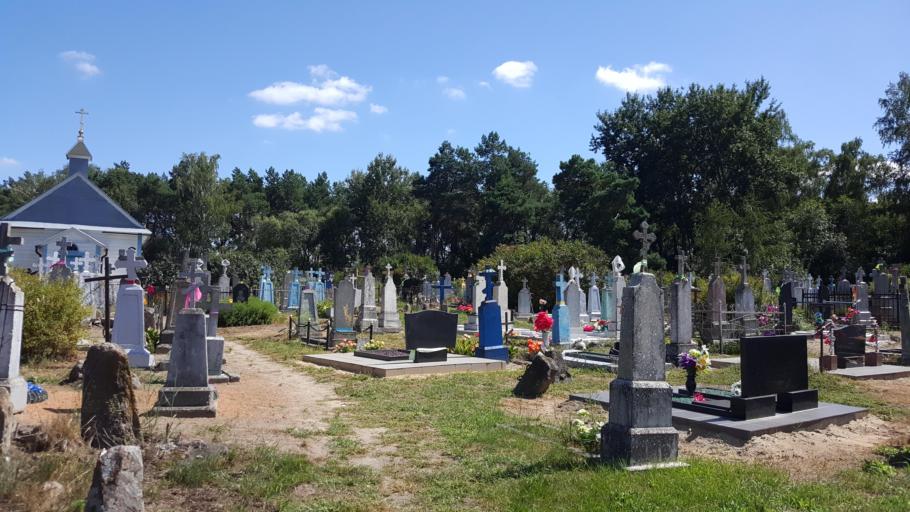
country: BY
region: Brest
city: Horad Kobryn
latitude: 52.2985
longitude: 24.3594
